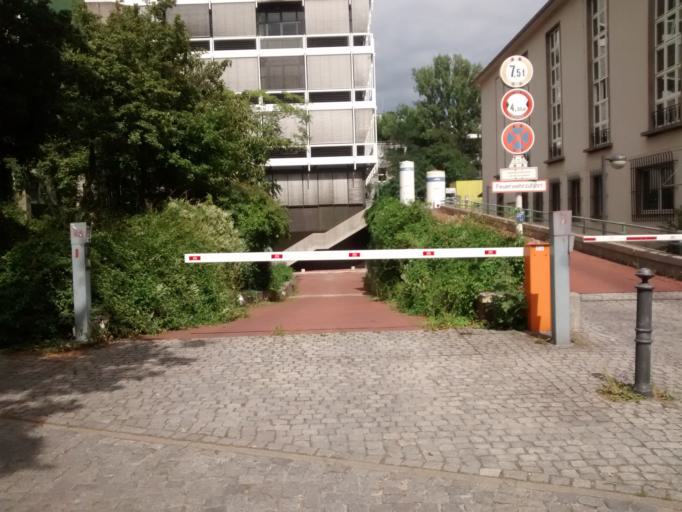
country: DE
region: Berlin
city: Hansaviertel
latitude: 52.5099
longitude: 13.3251
